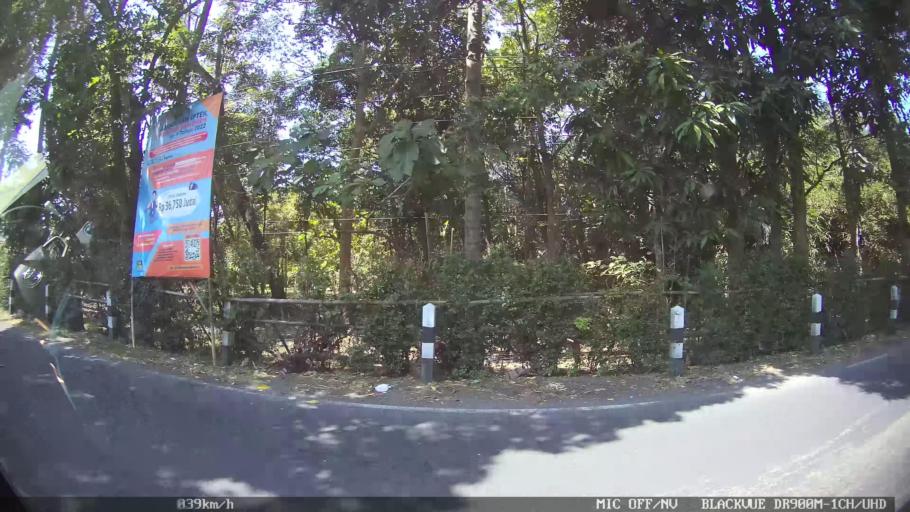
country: ID
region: Daerah Istimewa Yogyakarta
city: Srandakan
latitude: -7.9410
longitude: 110.2333
